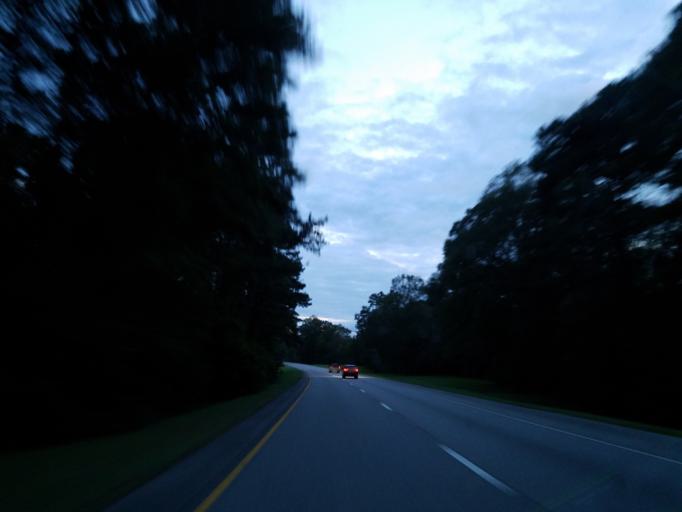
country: US
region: Mississippi
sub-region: Clarke County
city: Stonewall
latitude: 32.1795
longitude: -88.8641
